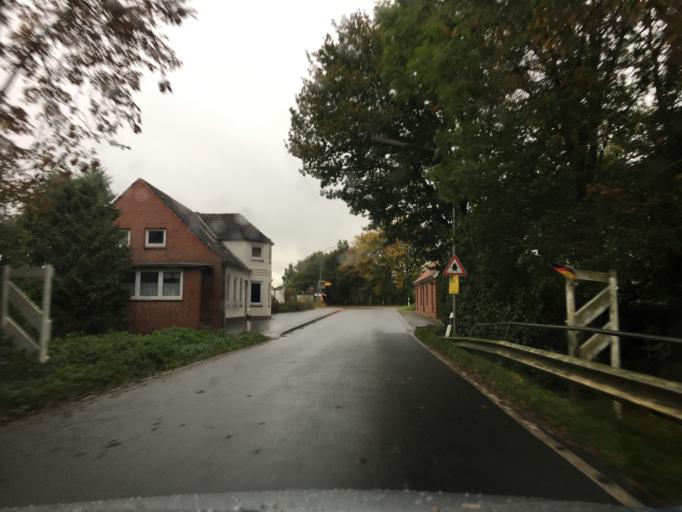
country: DE
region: Schleswig-Holstein
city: Quarnbek
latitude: 54.3292
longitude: 9.9832
